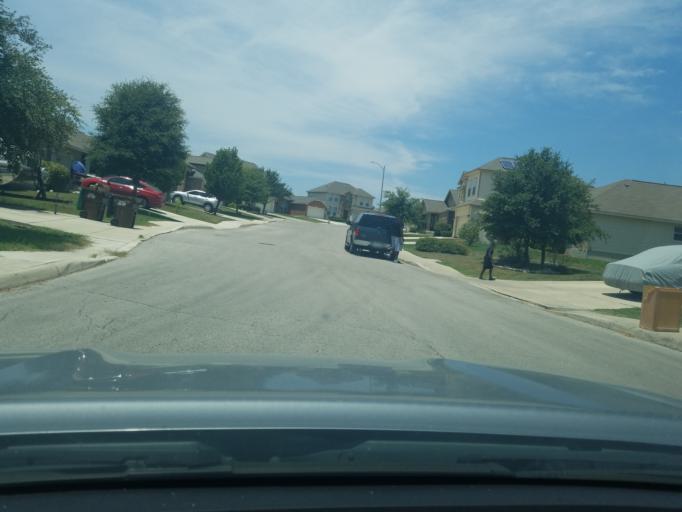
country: US
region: Texas
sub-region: Bexar County
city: Kirby
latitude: 29.4644
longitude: -98.3308
